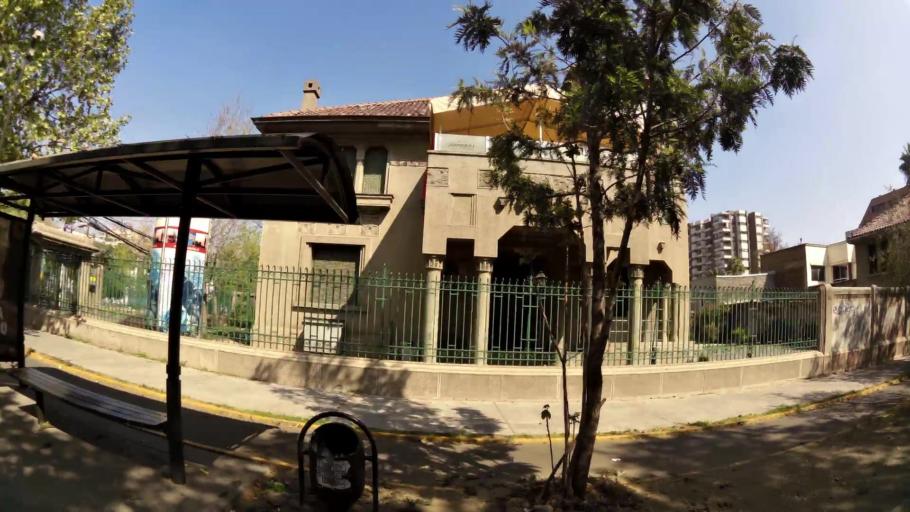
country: CL
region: Santiago Metropolitan
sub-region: Provincia de Santiago
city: Villa Presidente Frei, Nunoa, Santiago, Chile
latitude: -33.4552
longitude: -70.6094
